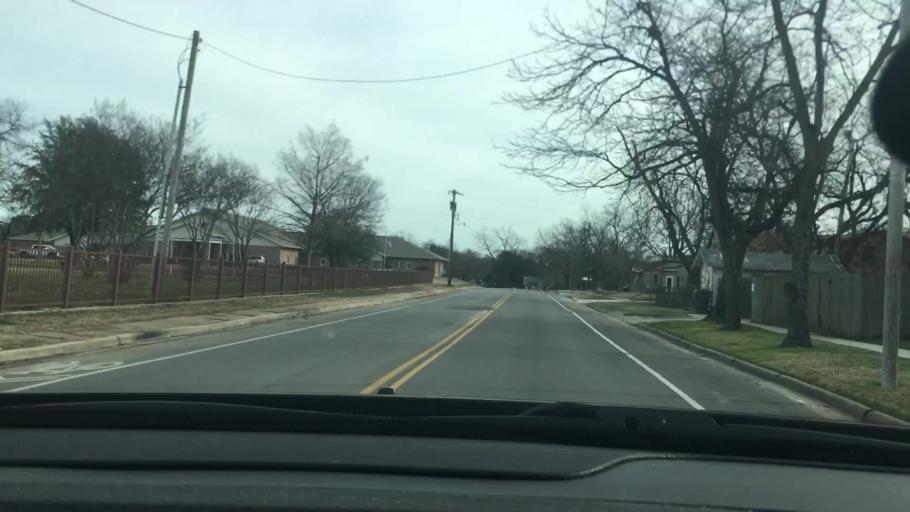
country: US
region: Oklahoma
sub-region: Carter County
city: Ardmore
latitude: 34.1766
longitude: -97.1201
